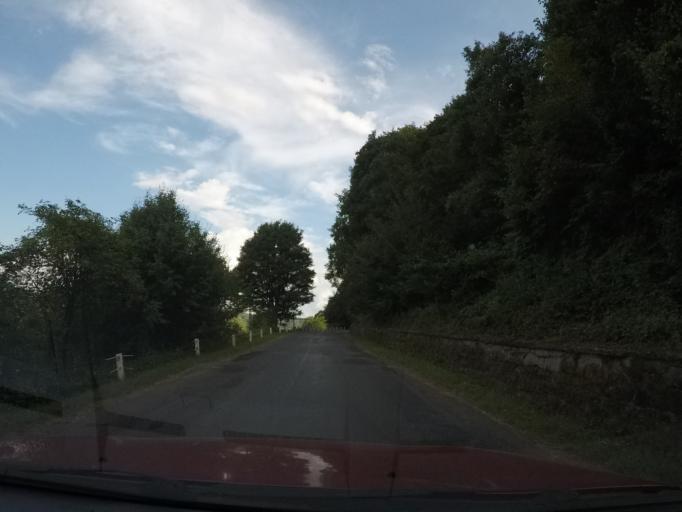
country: UA
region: Zakarpattia
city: Velykyi Bereznyi
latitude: 48.9189
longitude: 22.4564
